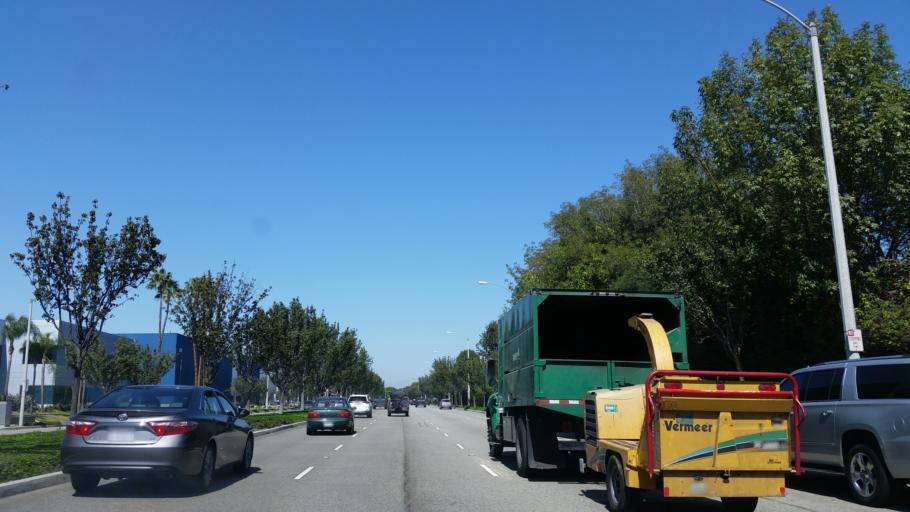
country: US
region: California
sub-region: Los Angeles County
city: Signal Hill
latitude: 33.8146
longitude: -118.1391
